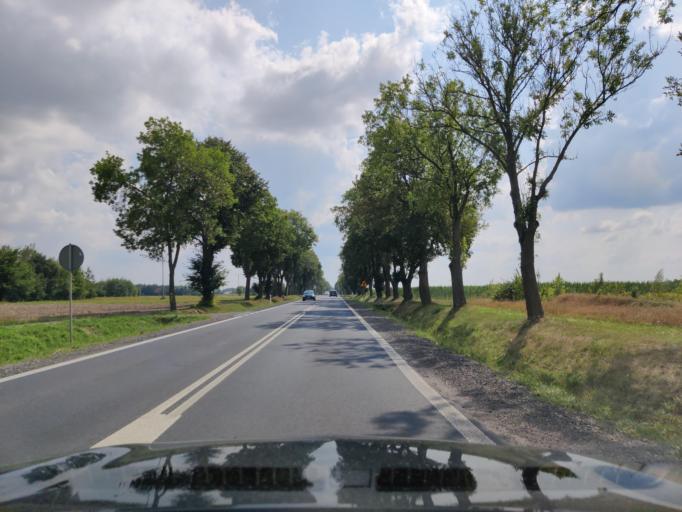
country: PL
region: Masovian Voivodeship
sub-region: Powiat pultuski
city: Zatory
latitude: 52.6150
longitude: 21.1040
